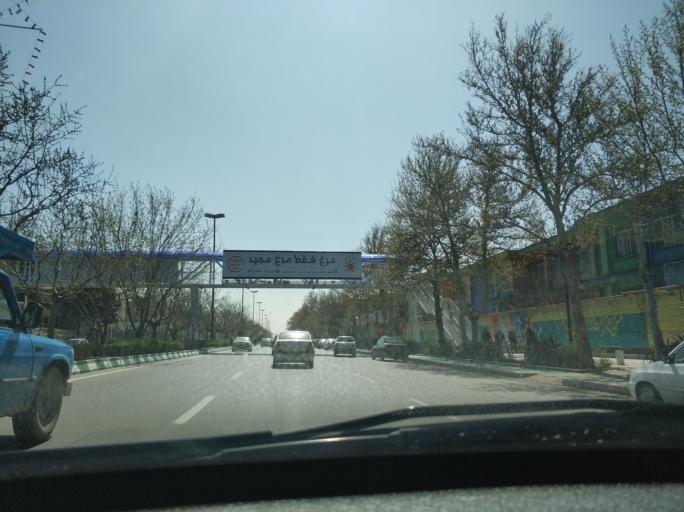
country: IR
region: Razavi Khorasan
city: Mashhad
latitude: 36.2609
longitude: 59.6058
